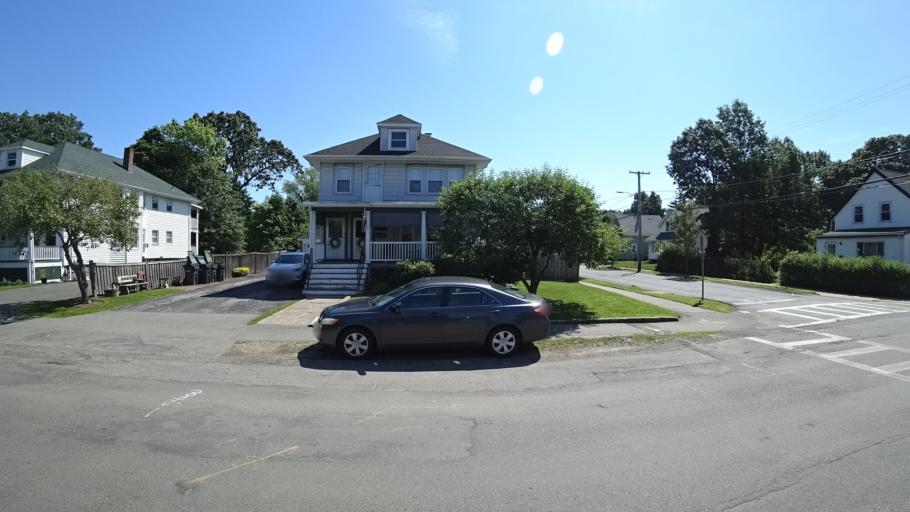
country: US
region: Massachusetts
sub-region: Norfolk County
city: Dedham
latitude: 42.2393
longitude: -71.1603
